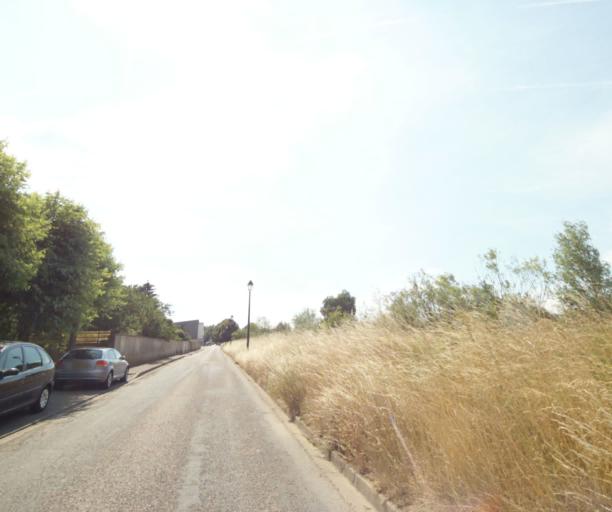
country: FR
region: Lorraine
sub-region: Departement de Meurthe-et-Moselle
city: Luneville
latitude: 48.5974
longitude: 6.4933
